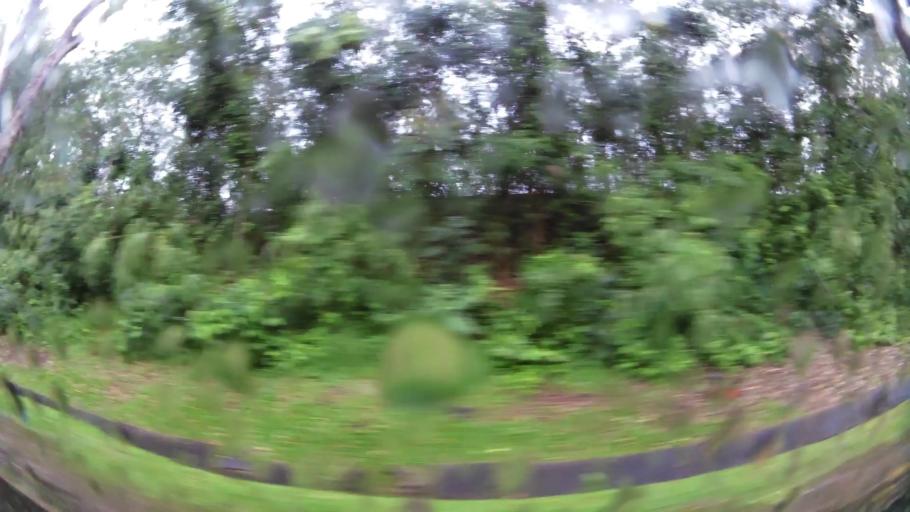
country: SG
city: Singapore
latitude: 1.3701
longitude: 103.9231
